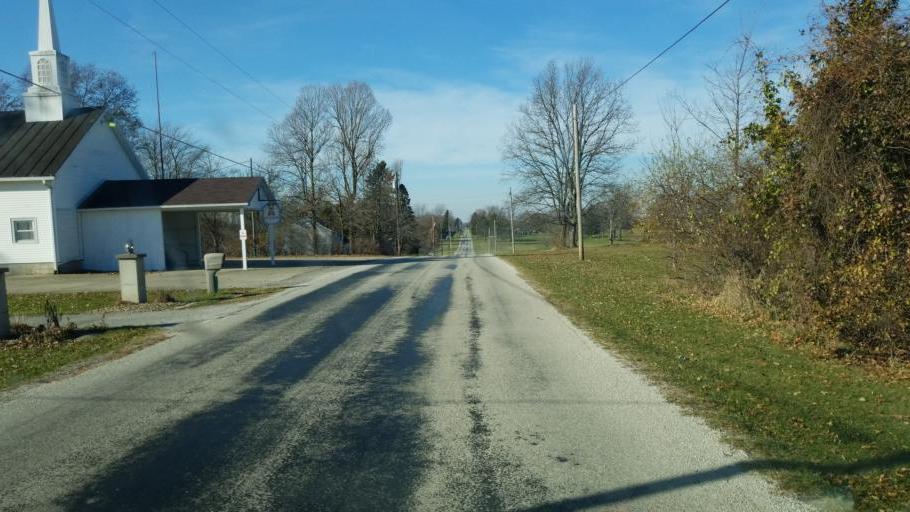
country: US
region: Ohio
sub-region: Richland County
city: Shelby
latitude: 40.8577
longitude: -82.5930
